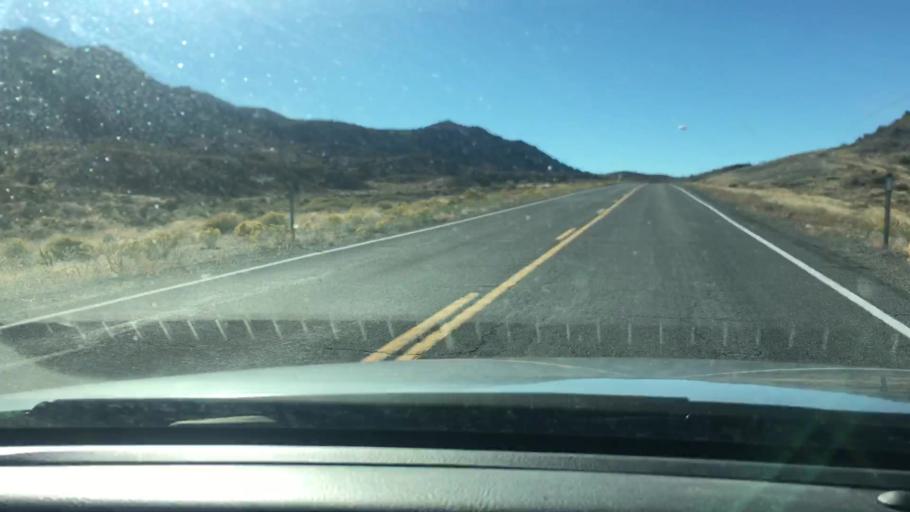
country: US
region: Nevada
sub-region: Nye County
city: Tonopah
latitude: 38.1716
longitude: -116.3916
